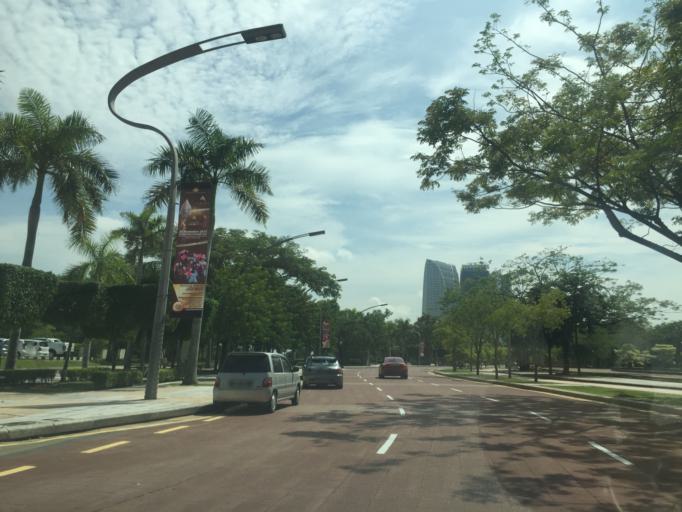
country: MY
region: Putrajaya
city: Putrajaya
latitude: 2.9123
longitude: 101.6835
